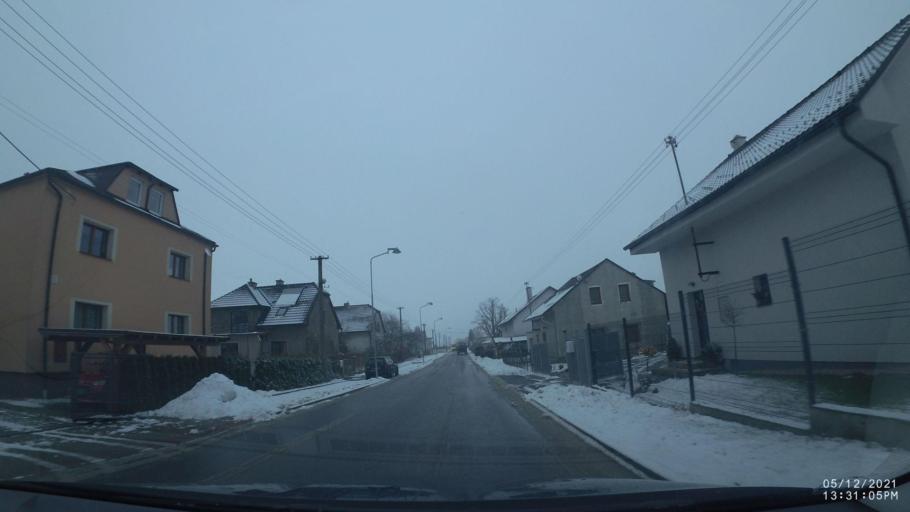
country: CZ
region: Kralovehradecky
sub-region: Okres Nachod
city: Police nad Metuji
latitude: 50.5076
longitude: 16.2303
